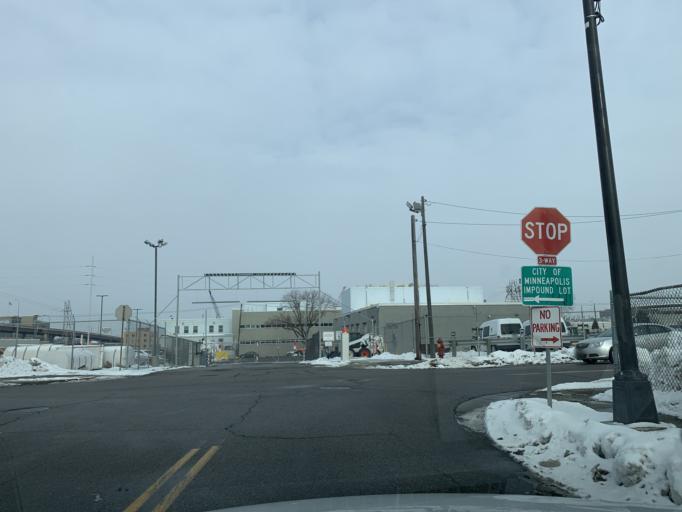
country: US
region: Minnesota
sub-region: Hennepin County
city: Minneapolis
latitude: 44.9758
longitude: -93.2856
